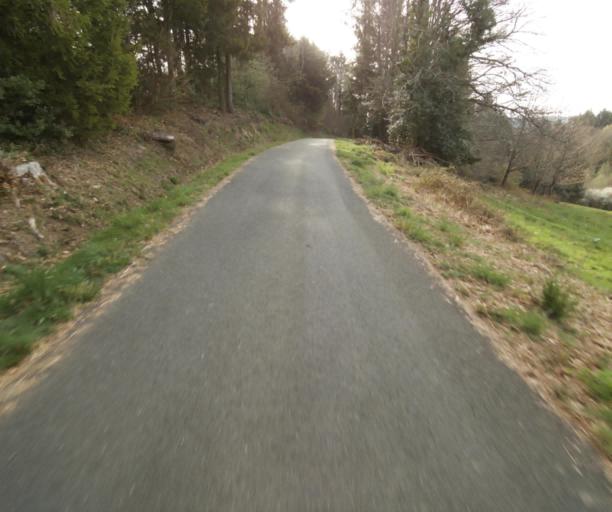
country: FR
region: Limousin
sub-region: Departement de la Correze
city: Chamboulive
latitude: 45.4358
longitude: 1.7849
